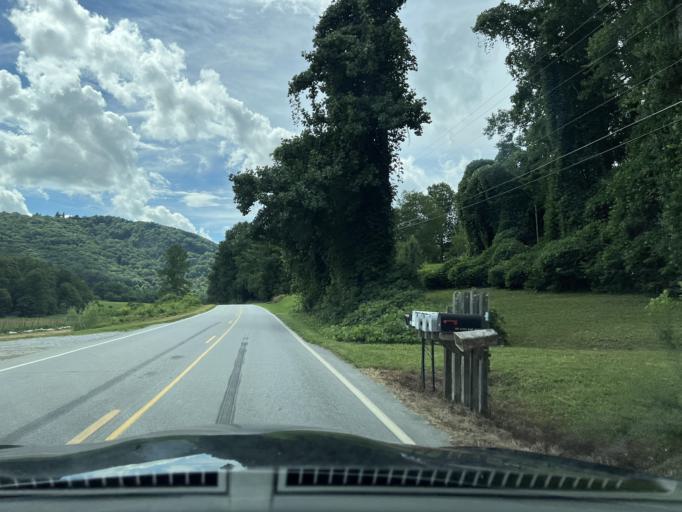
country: US
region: North Carolina
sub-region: Henderson County
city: Fruitland
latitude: 35.3986
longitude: -82.3988
